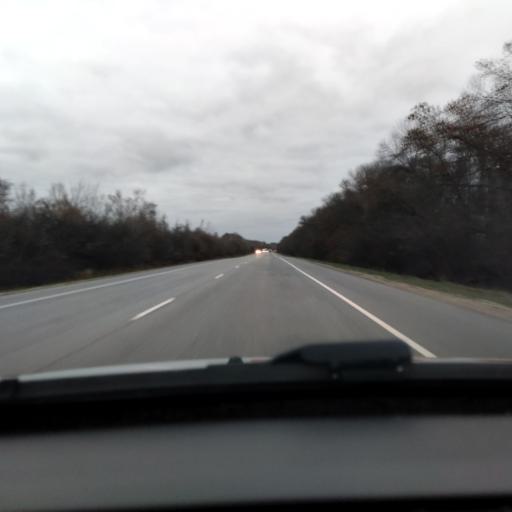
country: RU
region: Lipetsk
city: Borinskoye
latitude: 52.3631
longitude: 39.2026
